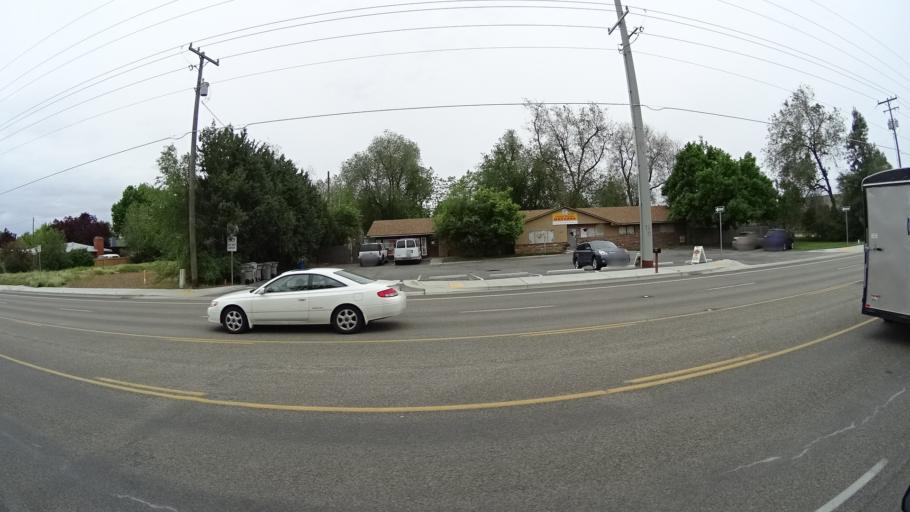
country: US
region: Idaho
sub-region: Ada County
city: Meridian
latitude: 43.6340
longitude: -116.3303
